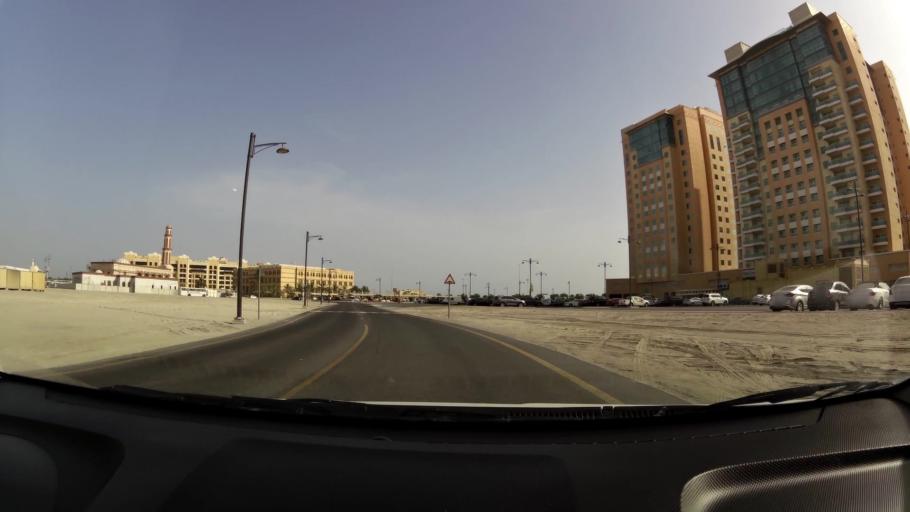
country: AE
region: Ash Shariqah
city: Sharjah
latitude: 25.2877
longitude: 55.3568
